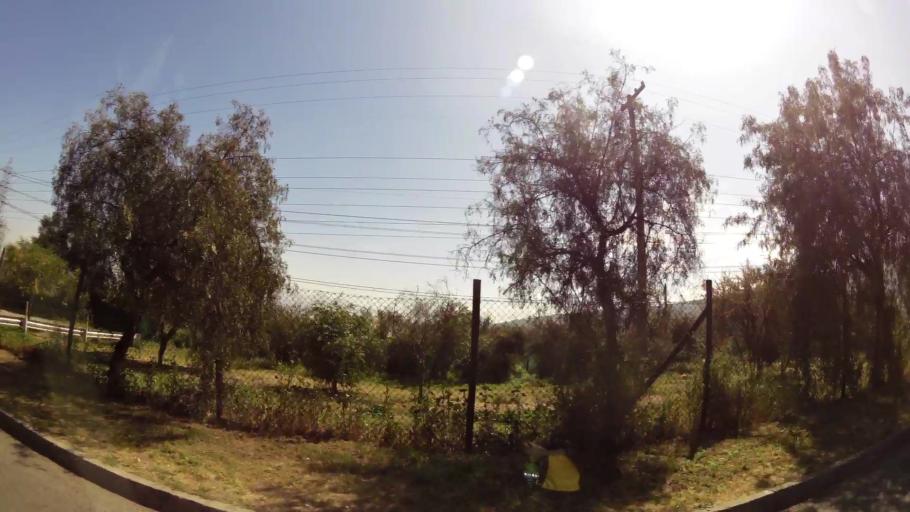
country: CL
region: Santiago Metropolitan
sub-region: Provincia de Santiago
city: Villa Presidente Frei, Nunoa, Santiago, Chile
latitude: -33.4318
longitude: -70.5251
